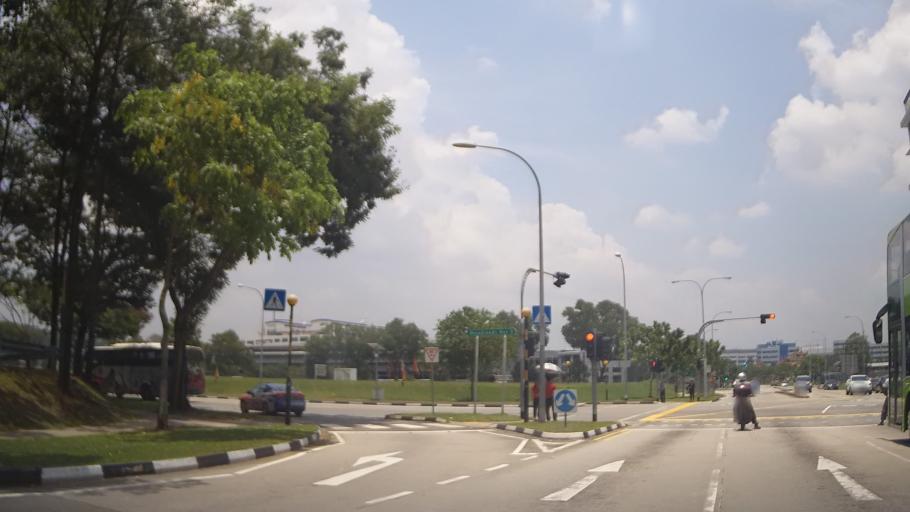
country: MY
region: Johor
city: Johor Bahru
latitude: 1.4472
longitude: 103.7971
